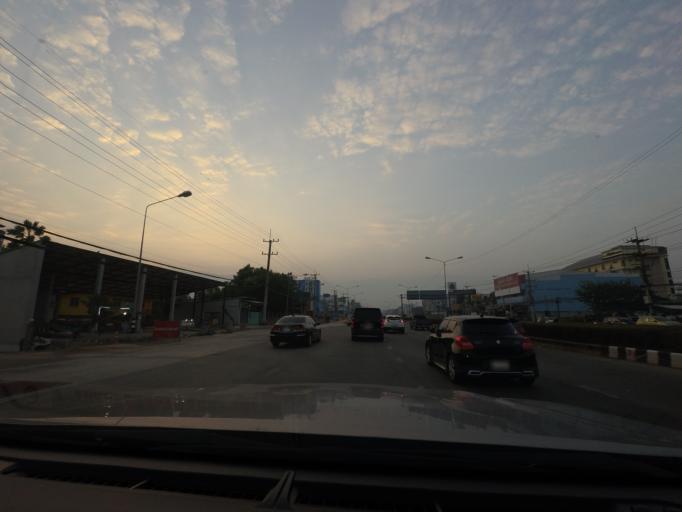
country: TH
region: Phitsanulok
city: Phitsanulok
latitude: 16.8183
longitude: 100.2881
